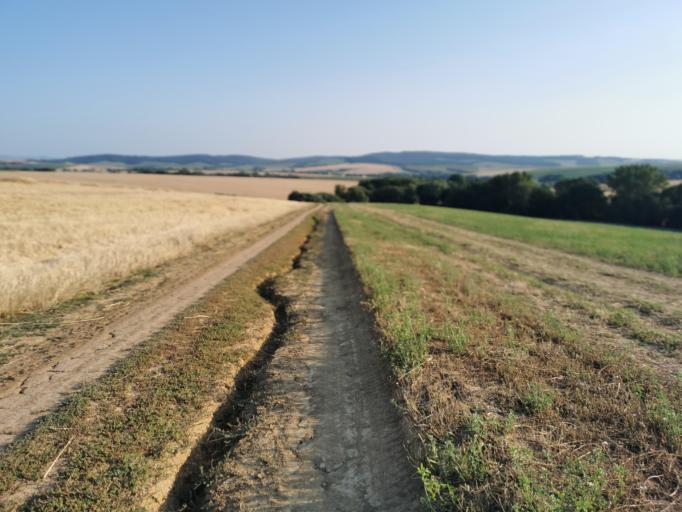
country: CZ
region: South Moravian
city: Sudomerice
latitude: 48.7957
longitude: 17.2914
